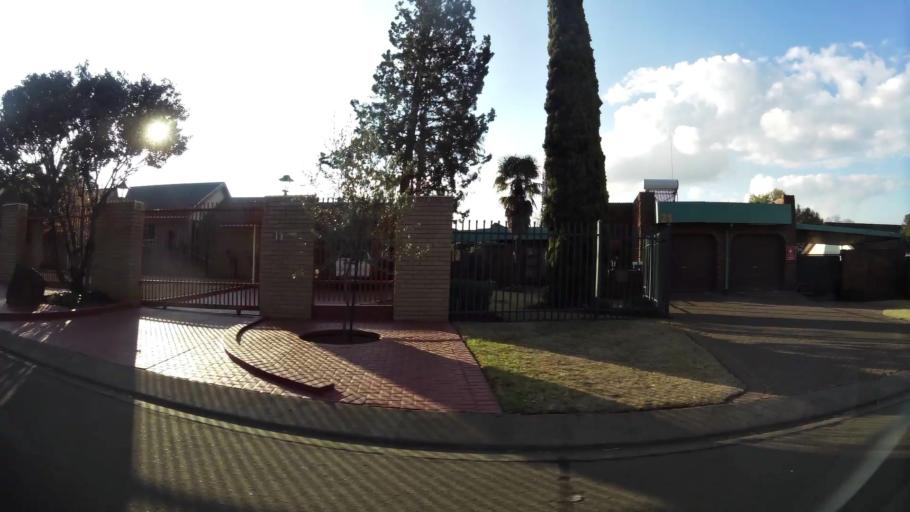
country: ZA
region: Orange Free State
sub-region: Mangaung Metropolitan Municipality
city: Bloemfontein
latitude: -29.1545
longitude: 26.1802
